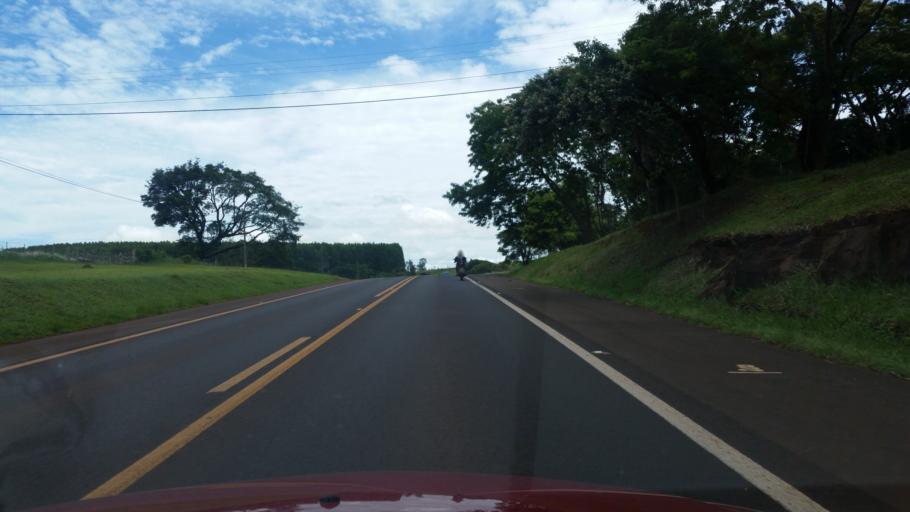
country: BR
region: Sao Paulo
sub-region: Itai
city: Itai
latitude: -23.3203
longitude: -49.0627
